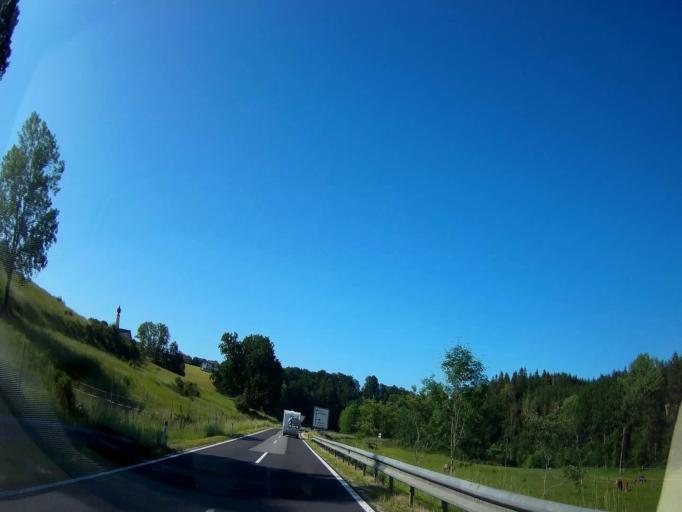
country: AT
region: Salzburg
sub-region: Politischer Bezirk Salzburg-Umgebung
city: Dorfbeuern
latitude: 48.1288
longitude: 13.0114
